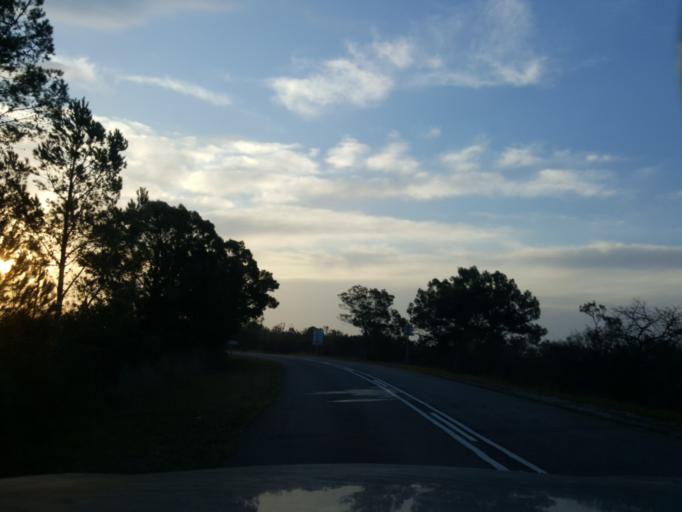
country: ZA
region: Eastern Cape
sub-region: Cacadu District Municipality
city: Grahamstown
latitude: -33.4576
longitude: 26.4972
